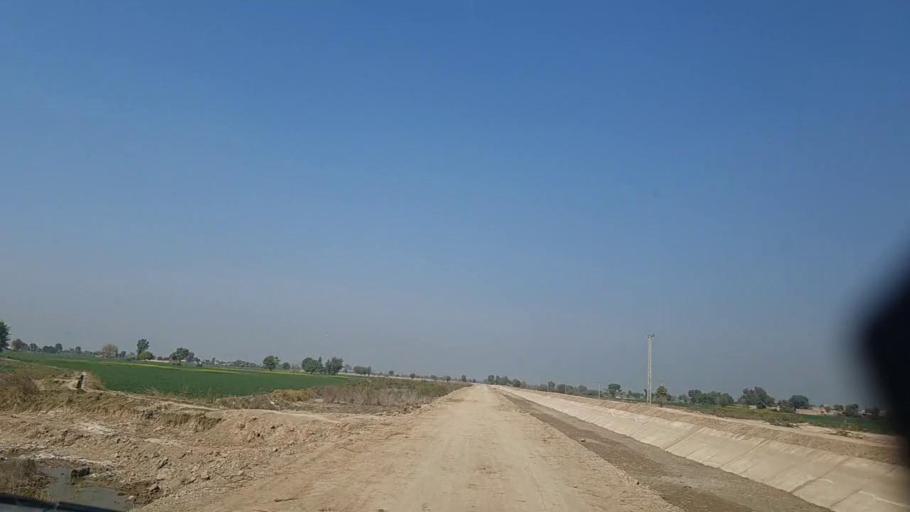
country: PK
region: Sindh
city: Sakrand
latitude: 26.1575
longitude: 68.3279
